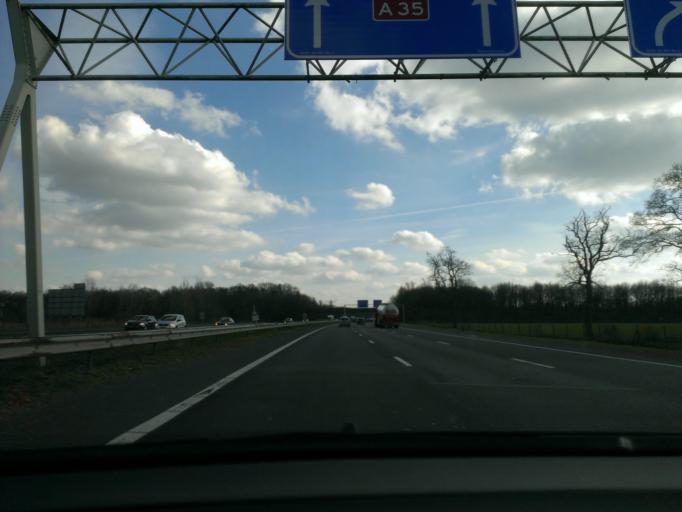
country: NL
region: Overijssel
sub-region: Gemeente Borne
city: Borne
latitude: 52.2768
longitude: 6.7483
